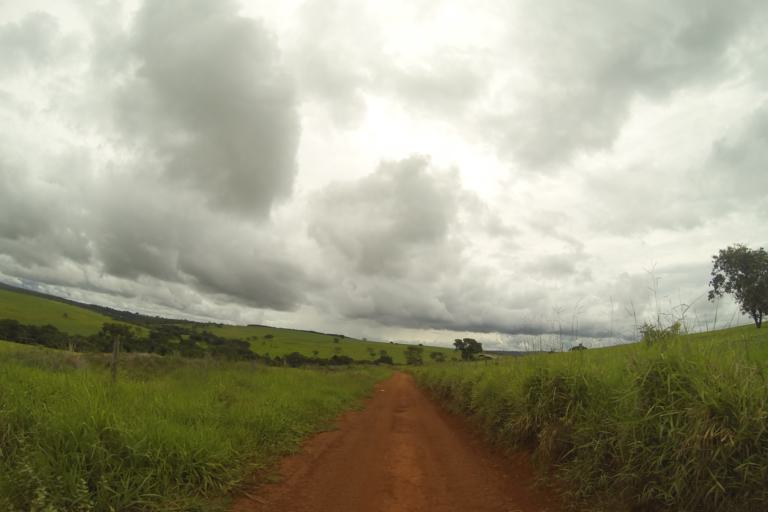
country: BR
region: Minas Gerais
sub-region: Ibia
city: Ibia
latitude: -19.7230
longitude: -46.5657
